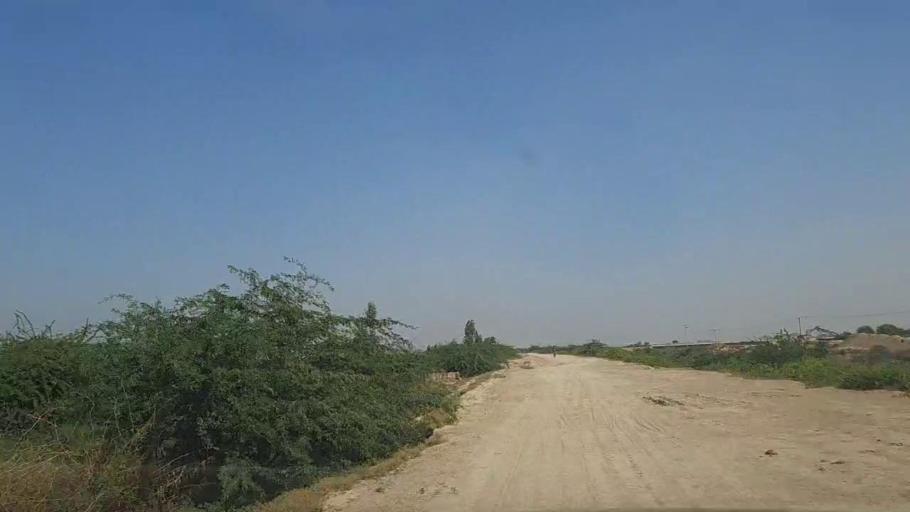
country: PK
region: Sindh
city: Daro Mehar
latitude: 24.8577
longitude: 68.0363
